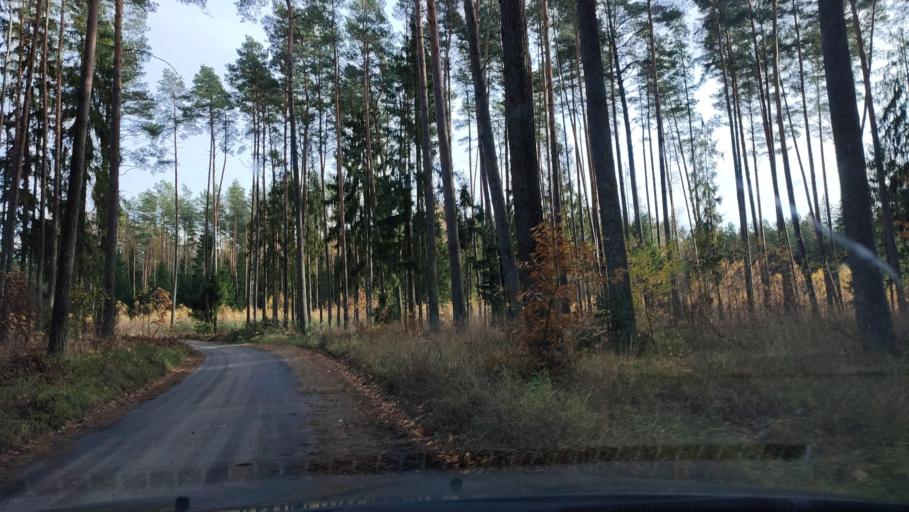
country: PL
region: Warmian-Masurian Voivodeship
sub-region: Powiat szczycienski
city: Szczytno
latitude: 53.5245
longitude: 20.8997
